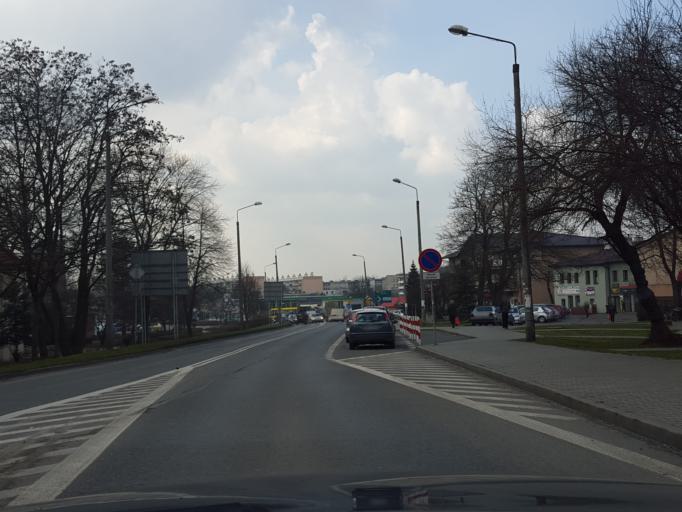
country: PL
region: Silesian Voivodeship
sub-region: Ruda Slaska
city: Ruda Slaska
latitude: 50.2432
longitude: 18.8398
